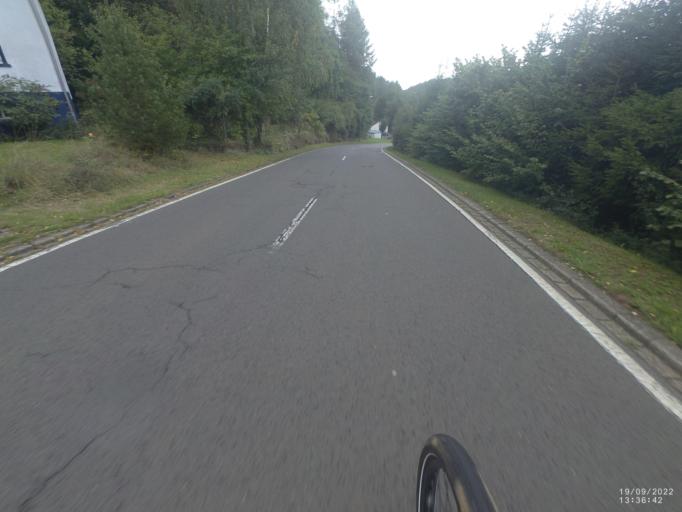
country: DE
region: Rheinland-Pfalz
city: Niederstadtfeld
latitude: 50.1612
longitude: 6.7656
